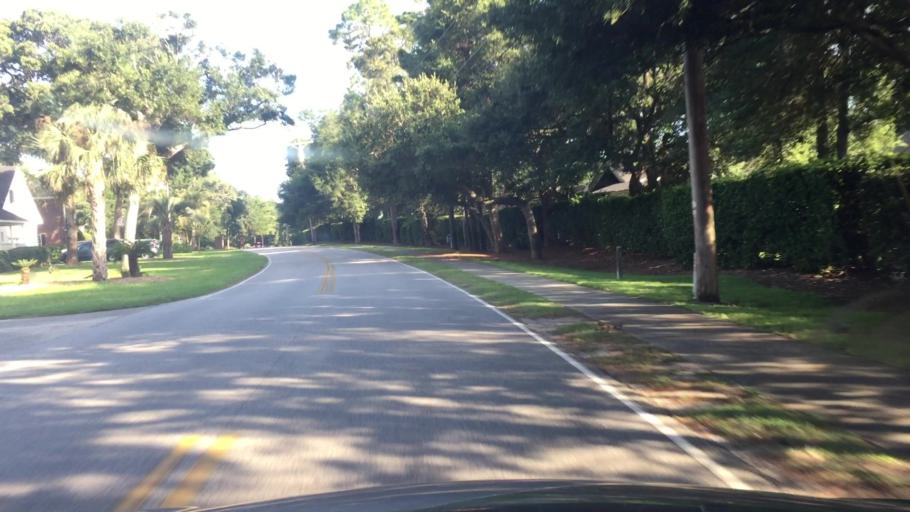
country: US
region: South Carolina
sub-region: Horry County
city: North Myrtle Beach
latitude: 33.8264
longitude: -78.6656
